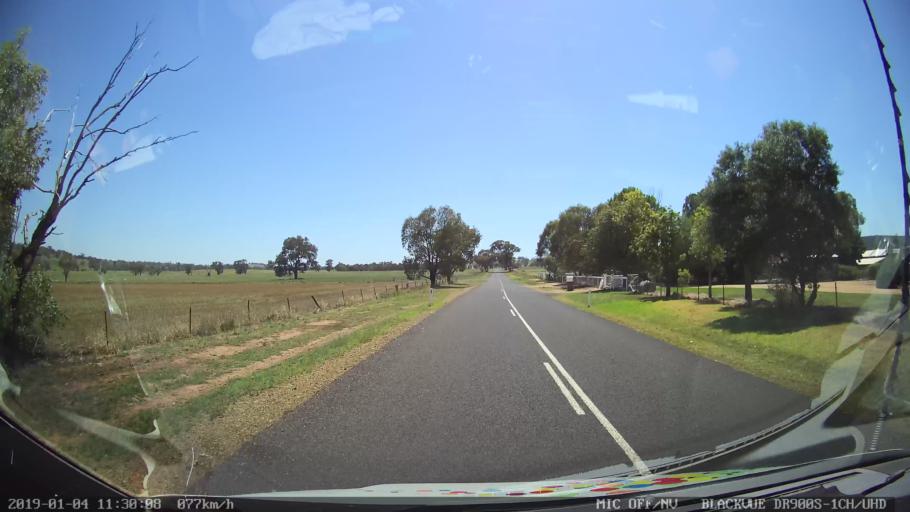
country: AU
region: New South Wales
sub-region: Cabonne
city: Molong
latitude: -33.0802
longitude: 148.7779
